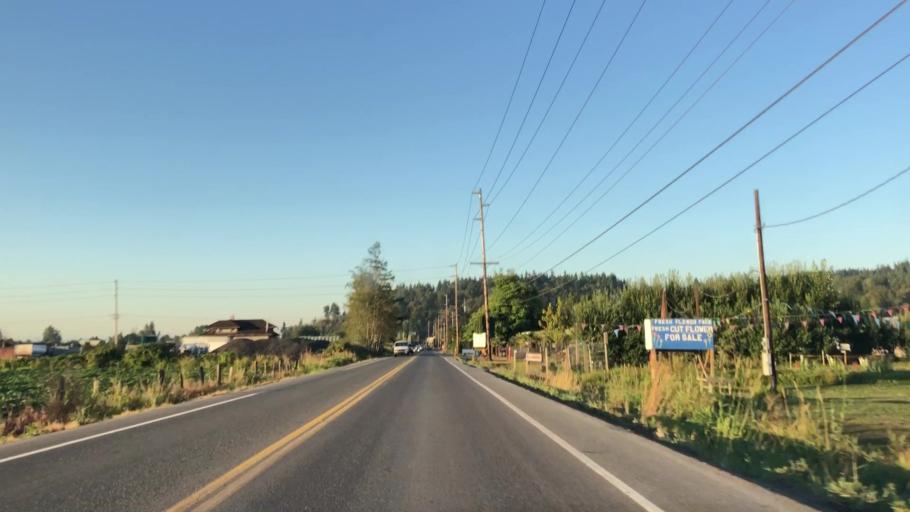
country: US
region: Washington
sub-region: King County
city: Lakeland North
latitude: 47.3480
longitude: -122.2497
